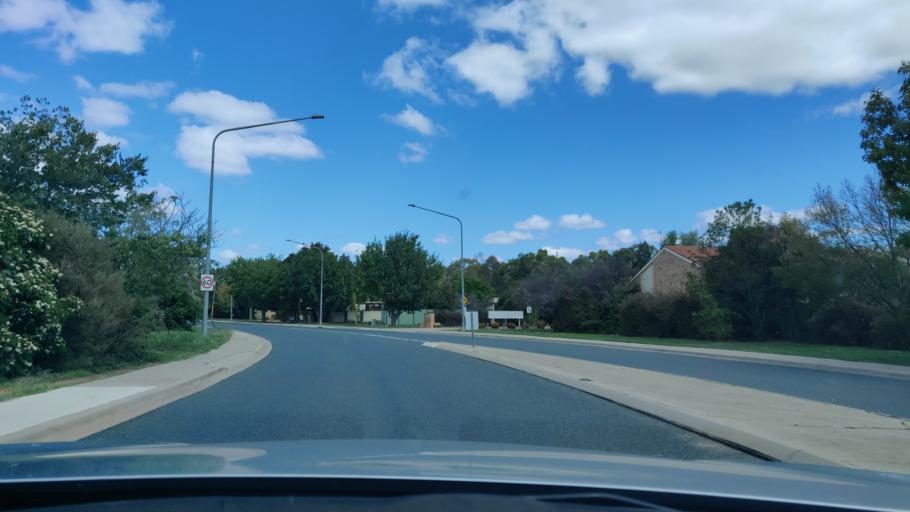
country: AU
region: Australian Capital Territory
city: Macarthur
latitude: -35.4297
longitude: 149.0884
